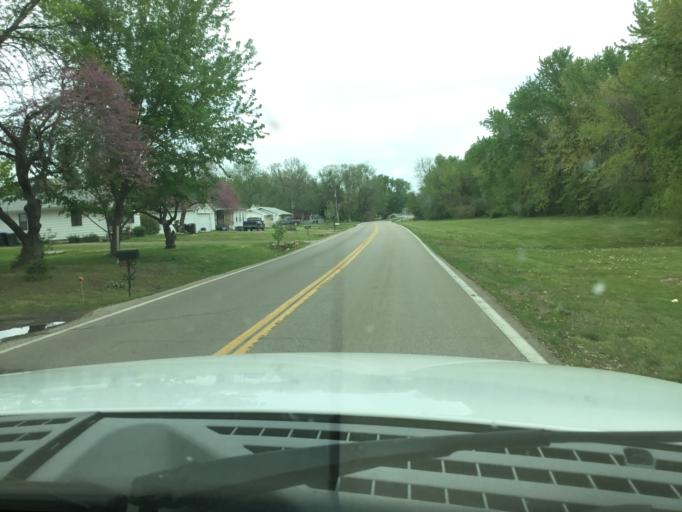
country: US
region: Kansas
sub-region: Shawnee County
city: Topeka
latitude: 39.0610
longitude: -95.6319
